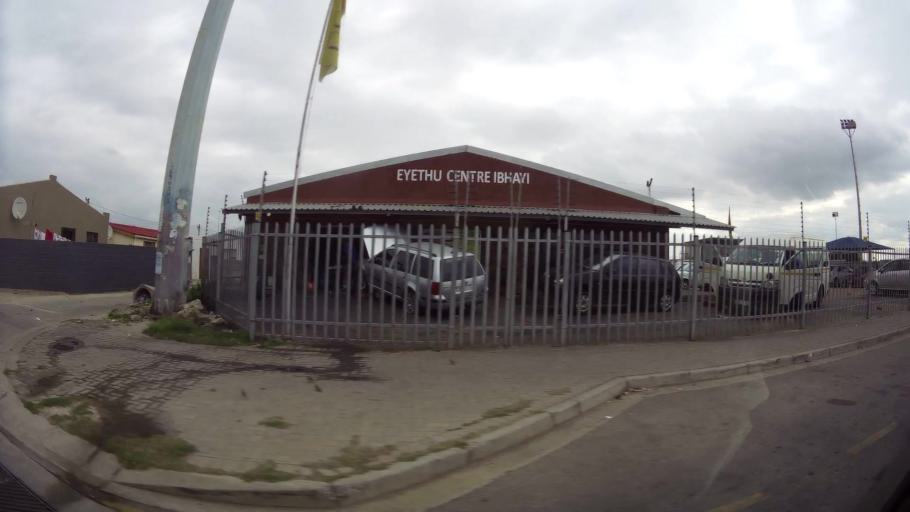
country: ZA
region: Eastern Cape
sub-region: Nelson Mandela Bay Metropolitan Municipality
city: Port Elizabeth
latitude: -33.8859
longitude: 25.5958
